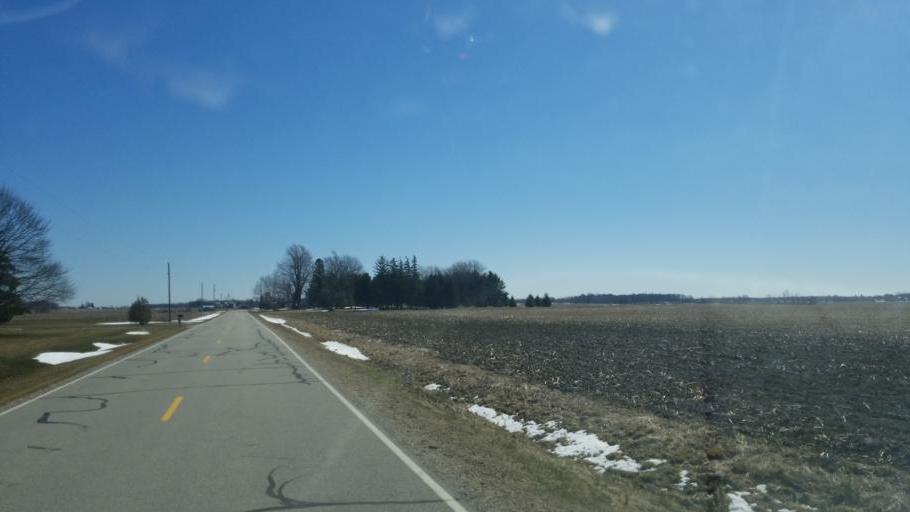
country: US
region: Ohio
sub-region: Crawford County
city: Bucyrus
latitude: 40.8046
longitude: -83.0800
